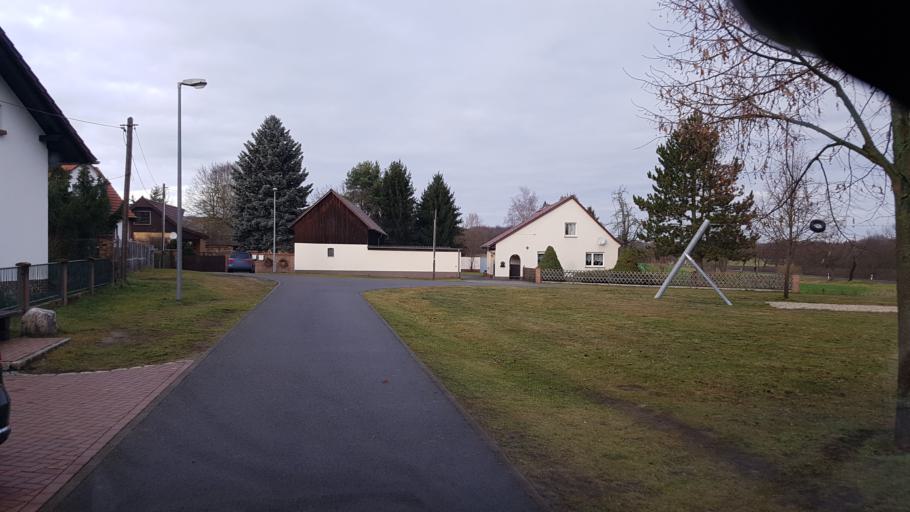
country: DE
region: Brandenburg
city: Altdobern
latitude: 51.6545
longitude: 13.9968
